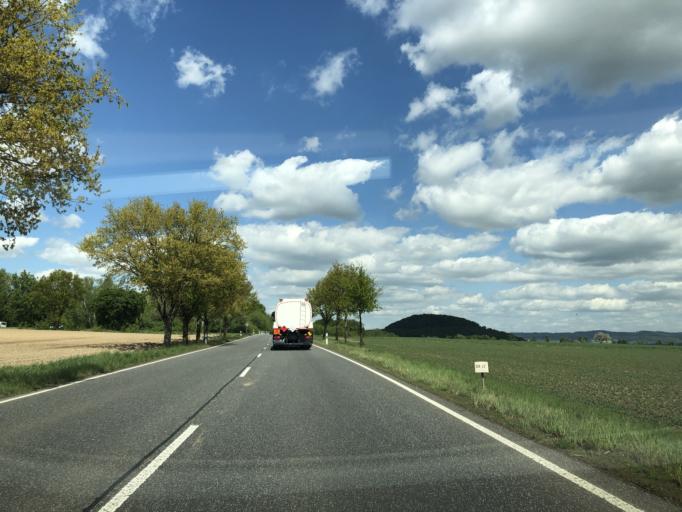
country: DE
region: Hesse
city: Gudensberg
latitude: 51.1708
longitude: 9.4035
